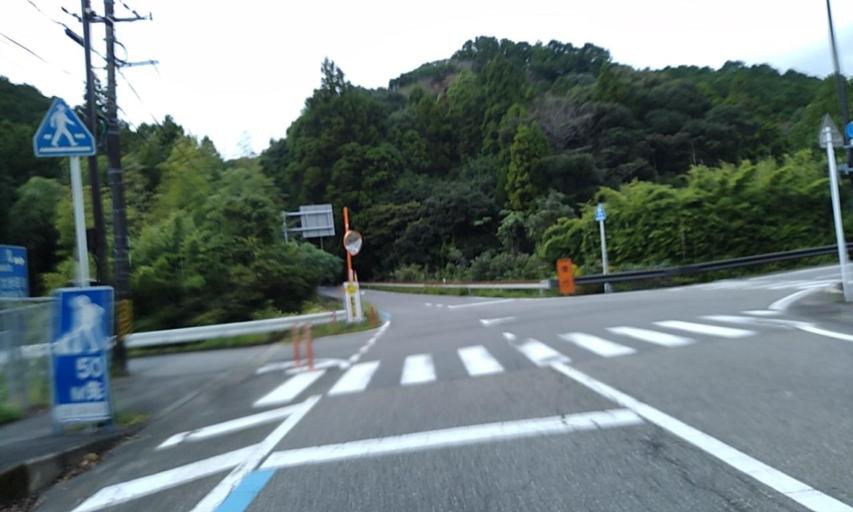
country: JP
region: Wakayama
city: Shingu
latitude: 33.5854
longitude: 135.9387
